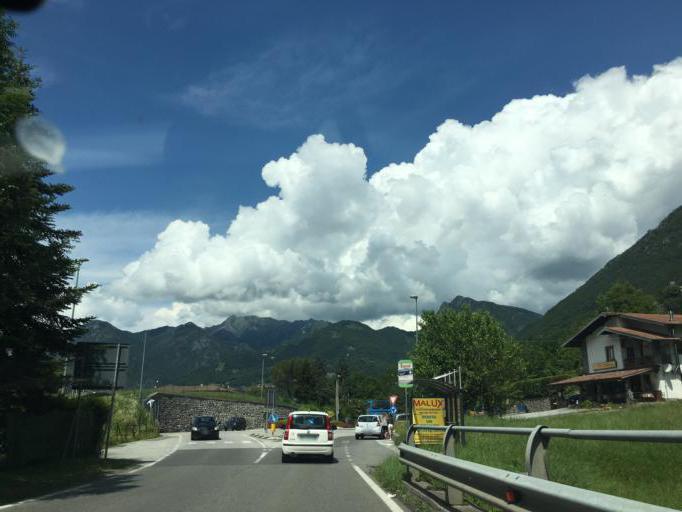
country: IT
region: Lombardy
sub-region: Provincia di Como
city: Bene Lario
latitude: 46.0381
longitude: 9.1794
